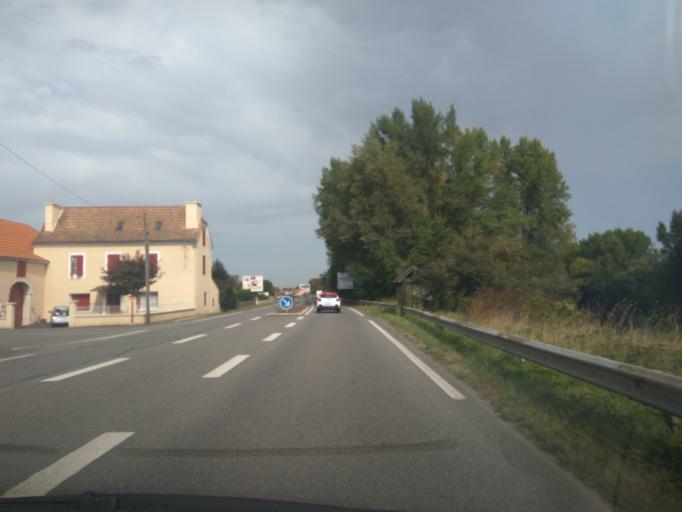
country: FR
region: Aquitaine
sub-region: Departement des Pyrenees-Atlantiques
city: Artiguelouve
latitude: 43.3114
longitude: -0.4499
